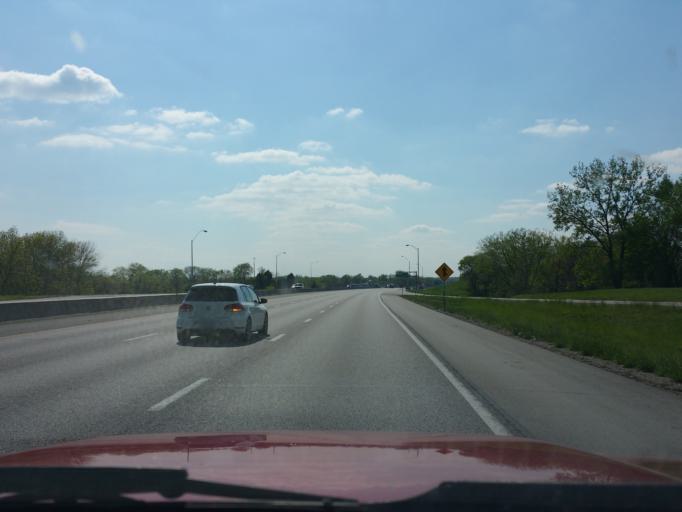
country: US
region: Kansas
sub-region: Johnson County
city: Shawnee
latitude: 39.1058
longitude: -94.7523
